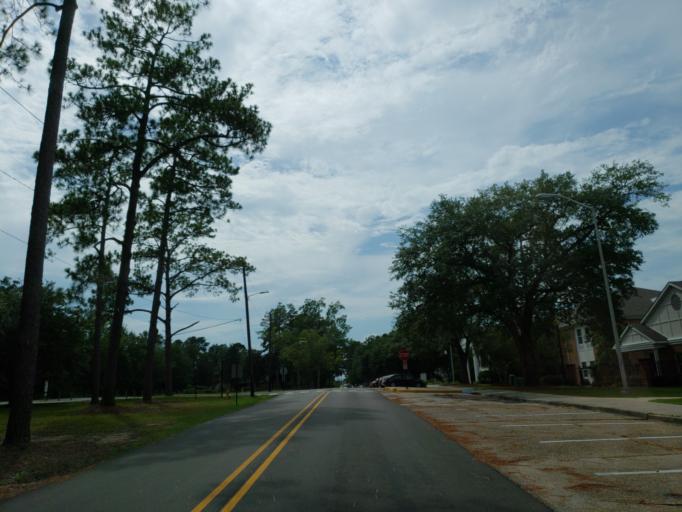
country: US
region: Mississippi
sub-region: Lamar County
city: Arnold Line
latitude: 31.3285
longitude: -89.3415
